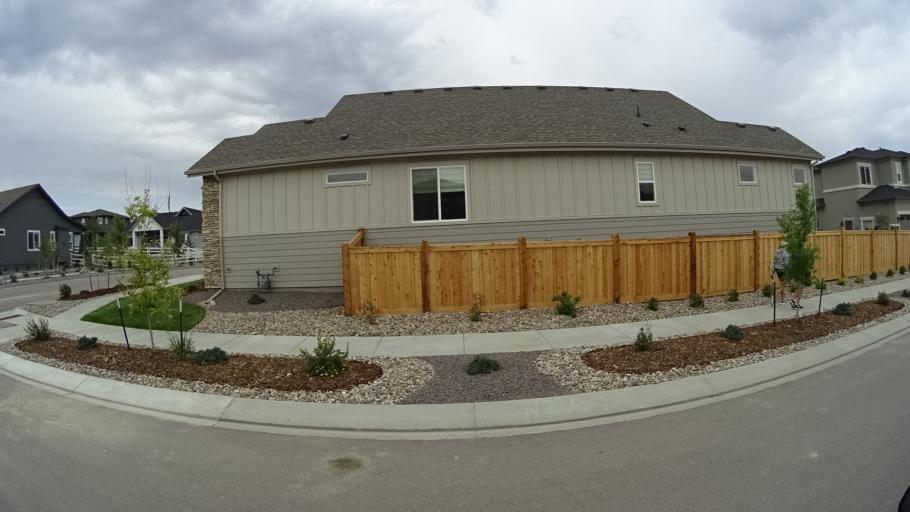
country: US
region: Colorado
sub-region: El Paso County
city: Gleneagle
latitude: 39.0044
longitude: -104.8094
